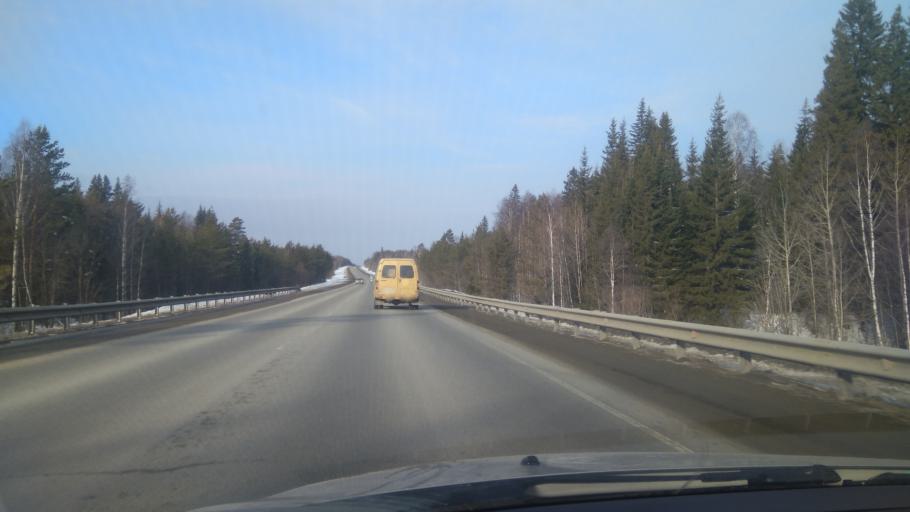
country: RU
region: Sverdlovsk
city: Nizhniye Sergi
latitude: 56.8249
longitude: 59.2699
